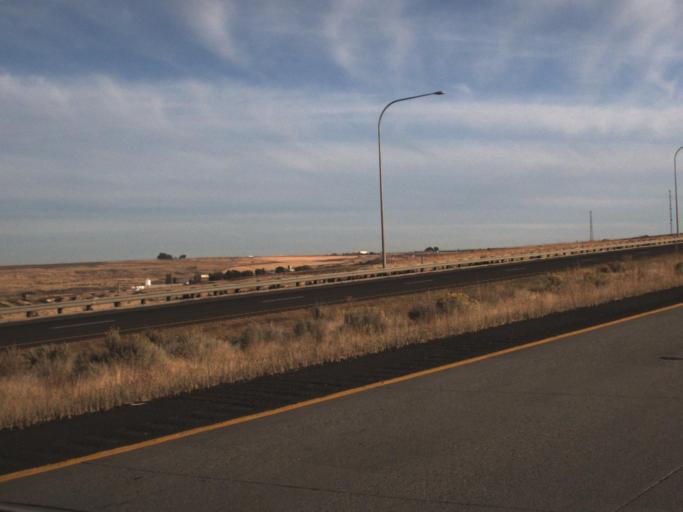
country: US
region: Washington
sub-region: Franklin County
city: Basin City
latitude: 46.5610
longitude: -118.9961
